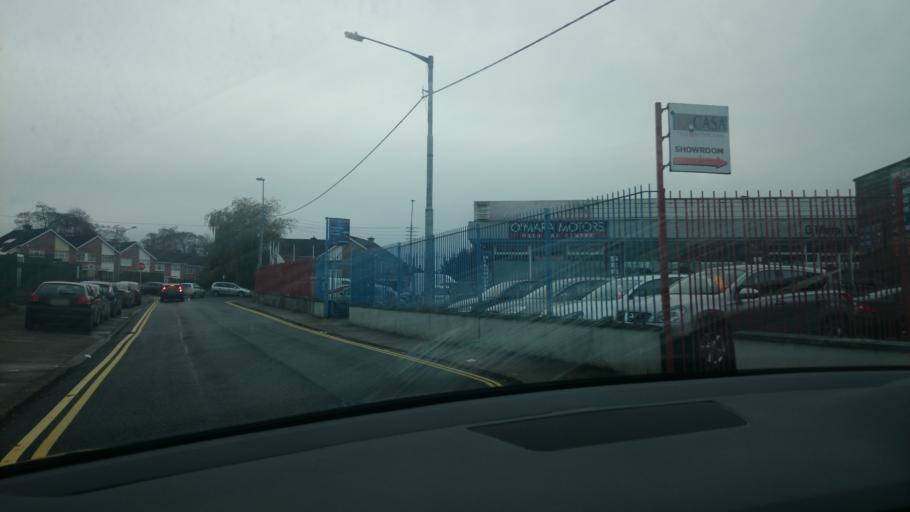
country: IE
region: Munster
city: Moyross
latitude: 52.6705
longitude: -8.6565
